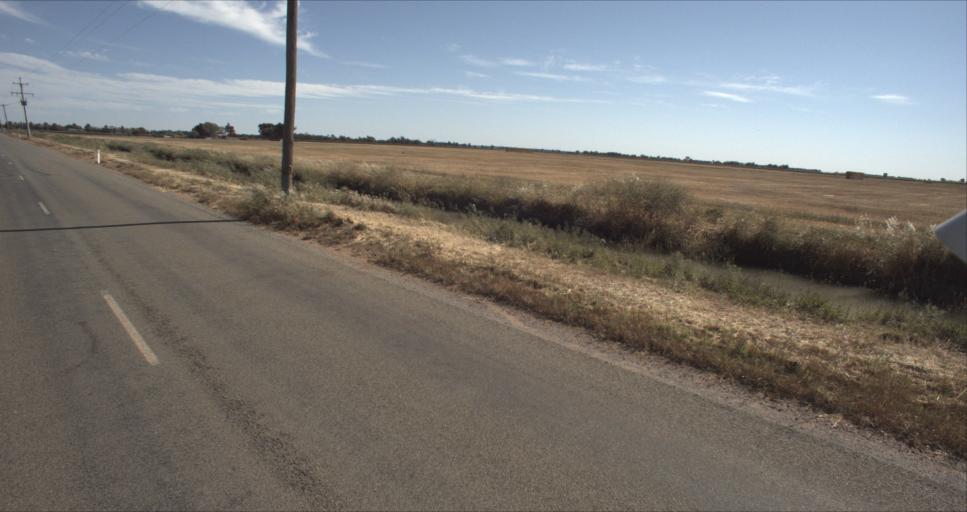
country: AU
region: New South Wales
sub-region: Leeton
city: Leeton
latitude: -34.5728
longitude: 146.3814
